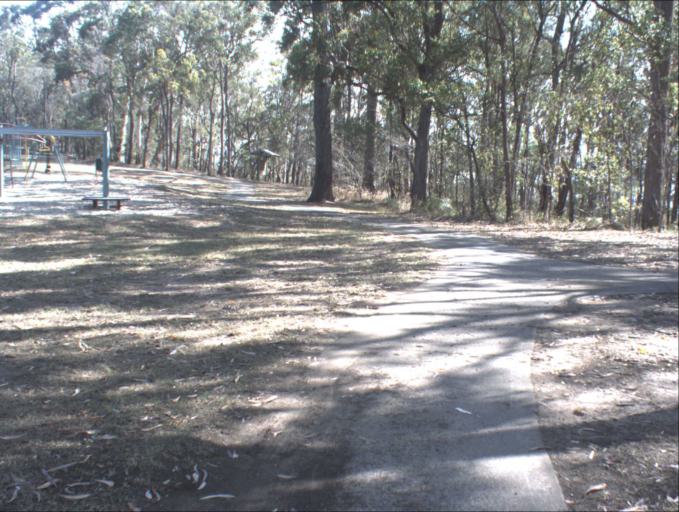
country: AU
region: Queensland
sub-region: Logan
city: Slacks Creek
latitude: -27.6440
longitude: 153.1868
